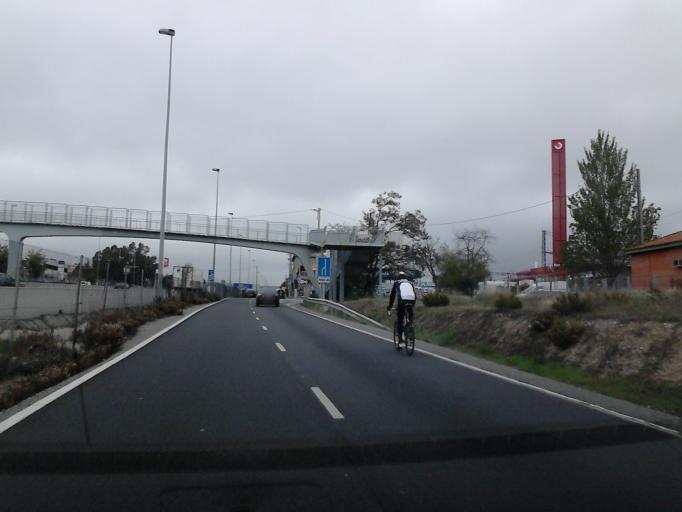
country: ES
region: Madrid
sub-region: Provincia de Madrid
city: Las Matas
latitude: 40.5513
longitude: -3.8970
